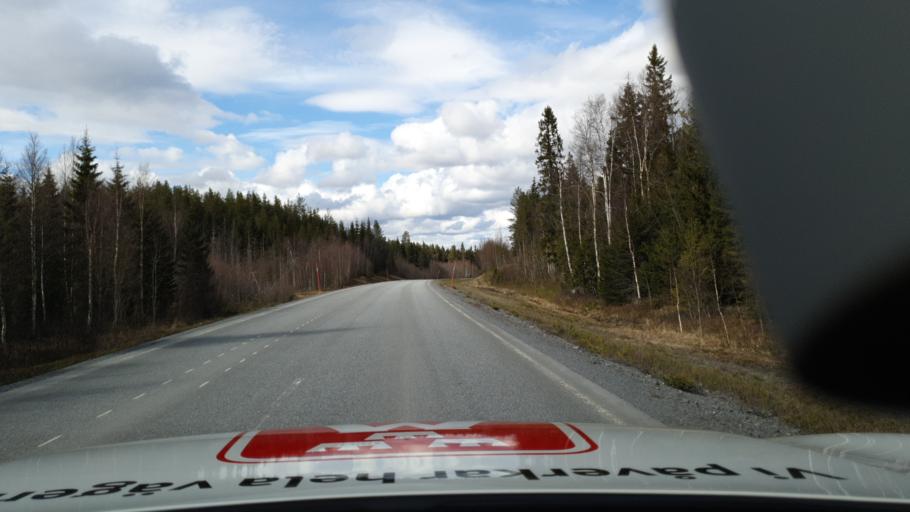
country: SE
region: Jaemtland
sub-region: Krokoms Kommun
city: Krokom
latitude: 63.3197
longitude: 14.4249
